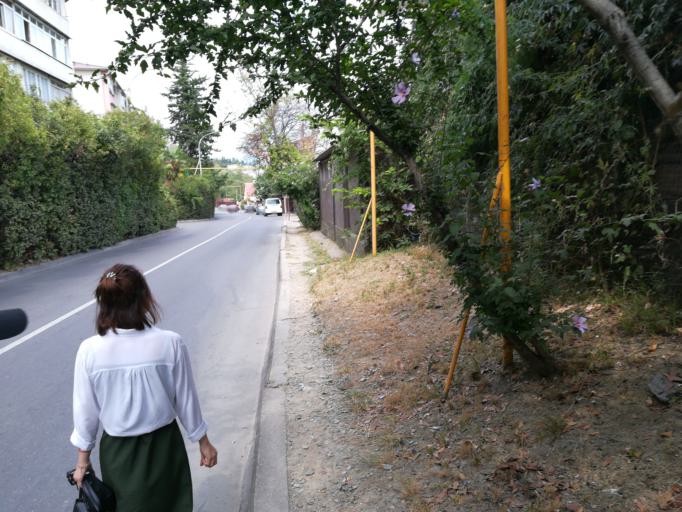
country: RU
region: Krasnodarskiy
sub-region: Sochi City
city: Sochi
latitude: 43.5924
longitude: 39.7414
